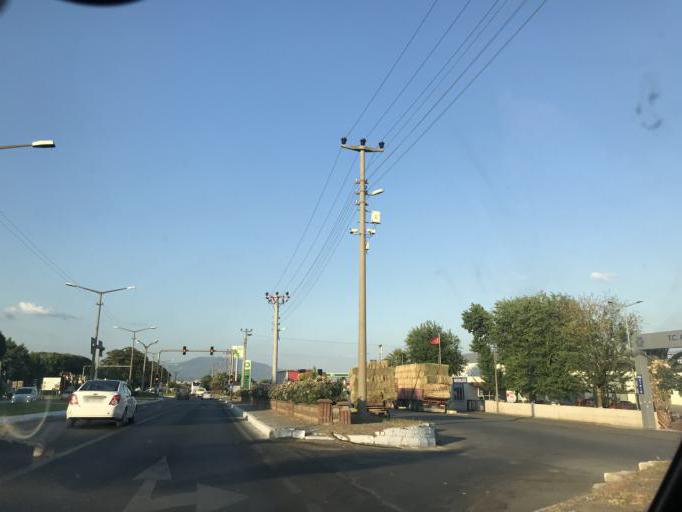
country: TR
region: Aydin
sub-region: Sultanhisar Ilcesi
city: Atca
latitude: 37.8843
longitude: 28.2163
